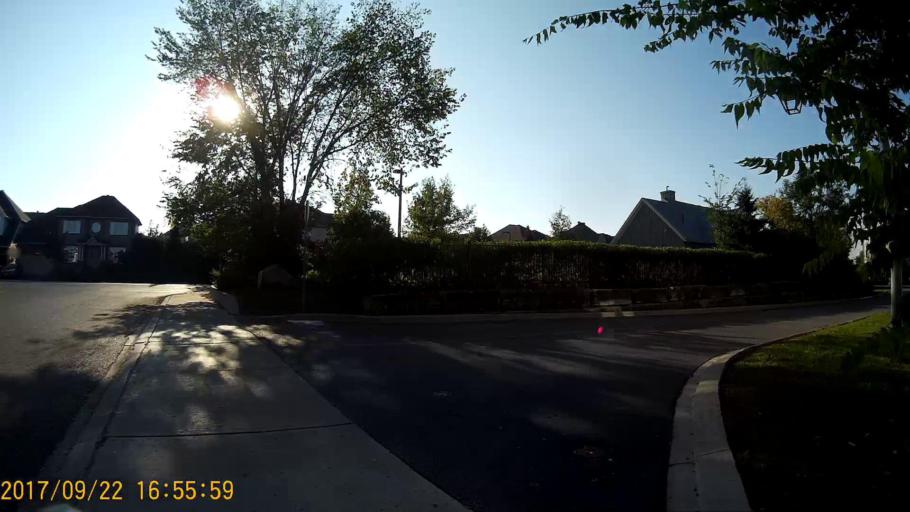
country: CA
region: Ontario
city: Bells Corners
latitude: 45.3528
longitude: -75.9335
